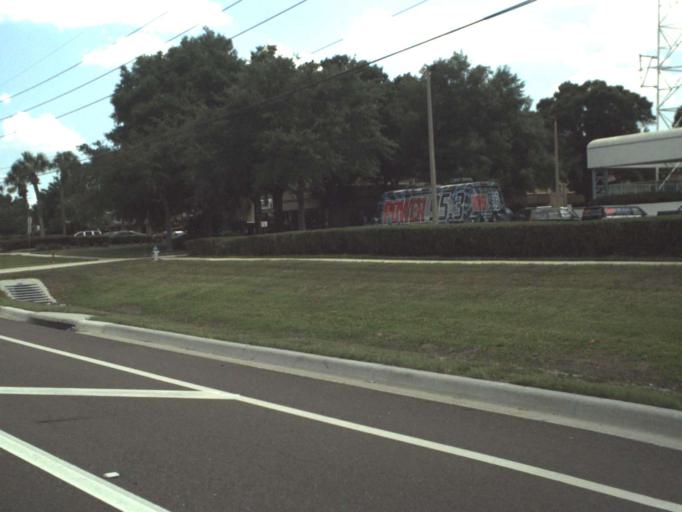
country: US
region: Florida
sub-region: Orange County
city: Fairview Shores
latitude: 28.5888
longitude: -81.4169
